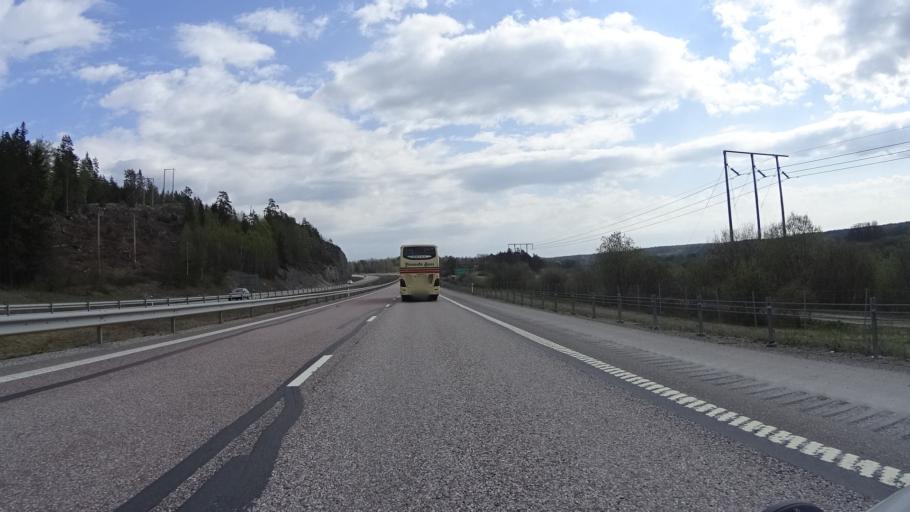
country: SE
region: Soedermanland
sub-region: Strangnas Kommun
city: Akers Styckebruk
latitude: 59.2570
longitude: 17.1488
